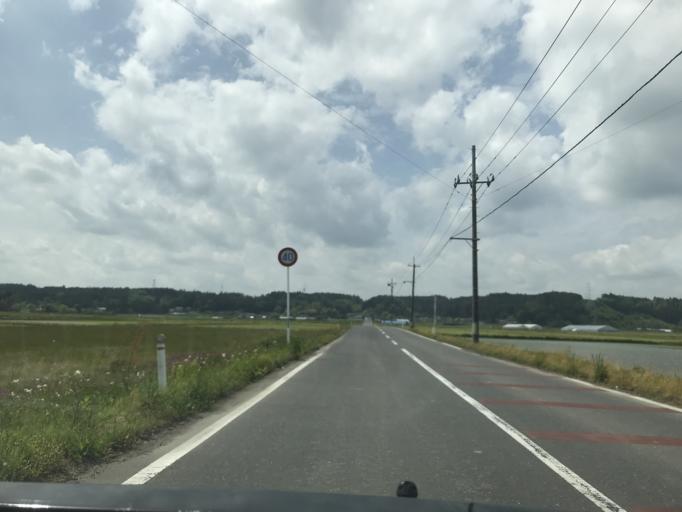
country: JP
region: Miyagi
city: Furukawa
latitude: 38.7476
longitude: 140.9341
